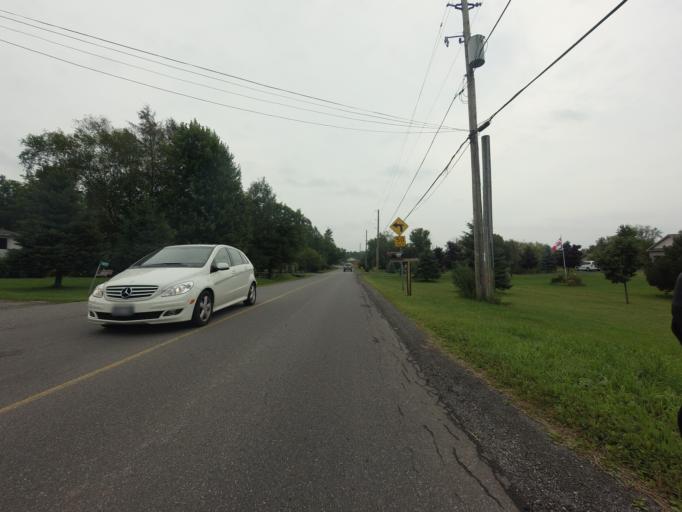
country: CA
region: Ontario
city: Bells Corners
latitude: 45.3394
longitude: -76.0008
